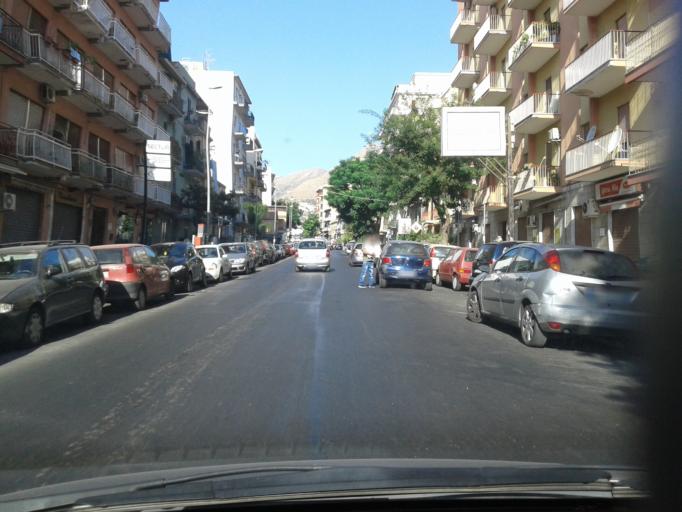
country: IT
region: Sicily
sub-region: Palermo
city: Palermo
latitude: 38.1106
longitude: 13.3266
